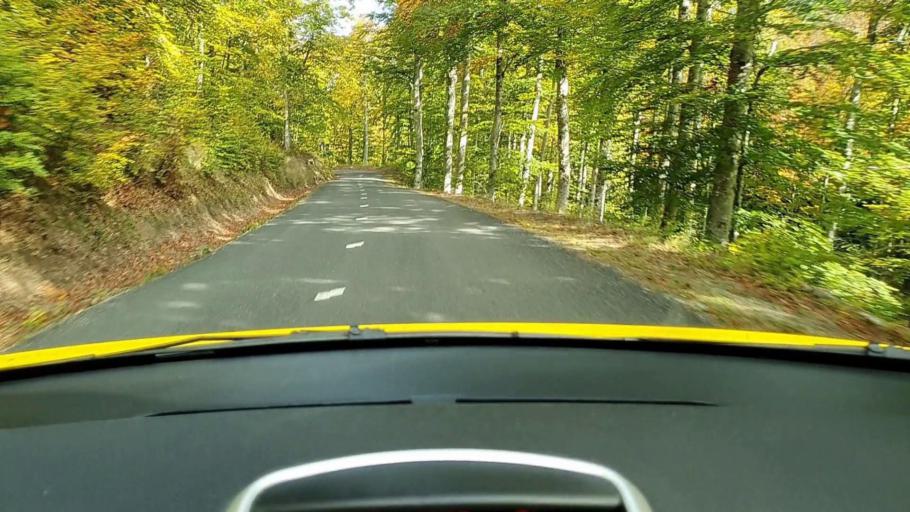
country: FR
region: Languedoc-Roussillon
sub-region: Departement du Gard
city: Valleraugue
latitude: 44.0694
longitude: 3.5683
